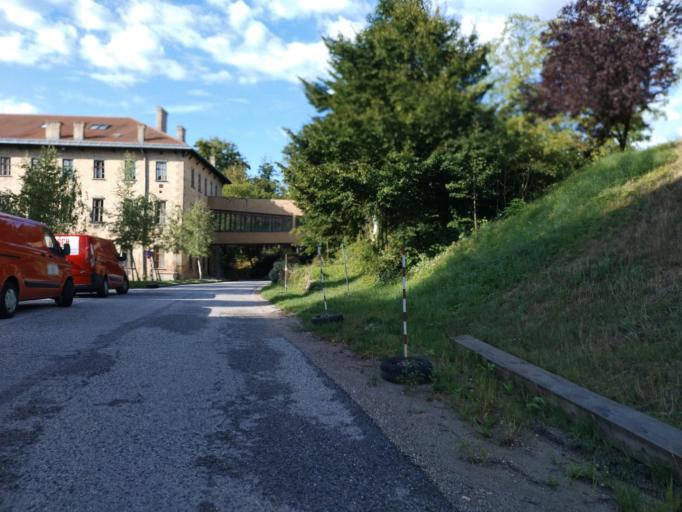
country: AT
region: Lower Austria
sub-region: Politischer Bezirk Wien-Umgebung
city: Pressbaum
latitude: 48.1859
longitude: 16.0814
